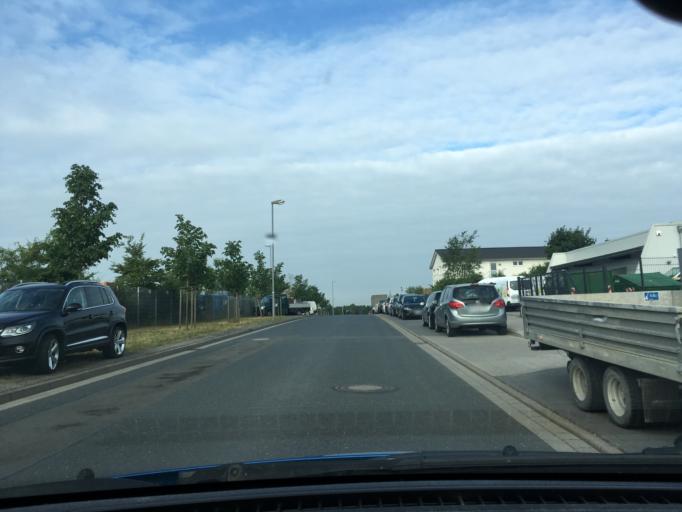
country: DE
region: Lower Saxony
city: Kakenstorf
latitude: 53.3229
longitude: 9.8151
